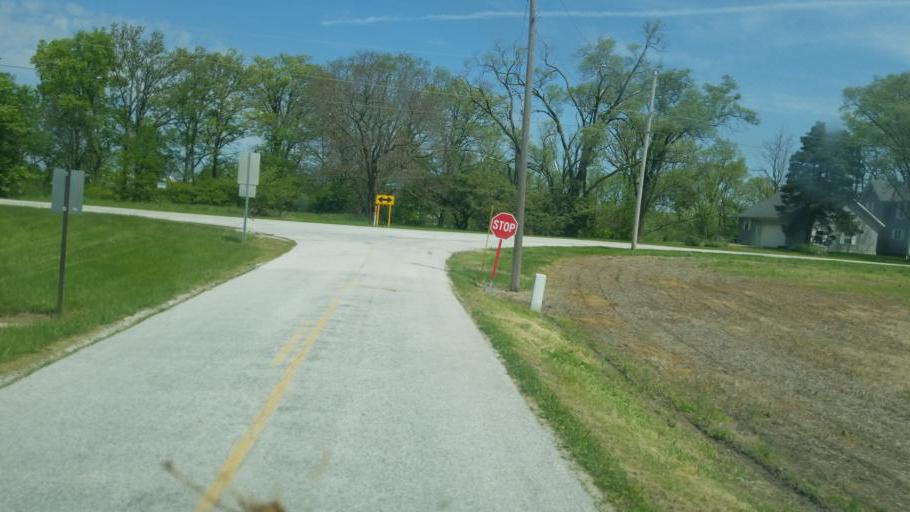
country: US
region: Ohio
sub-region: Ottawa County
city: Oak Harbor
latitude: 41.4943
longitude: -83.2022
